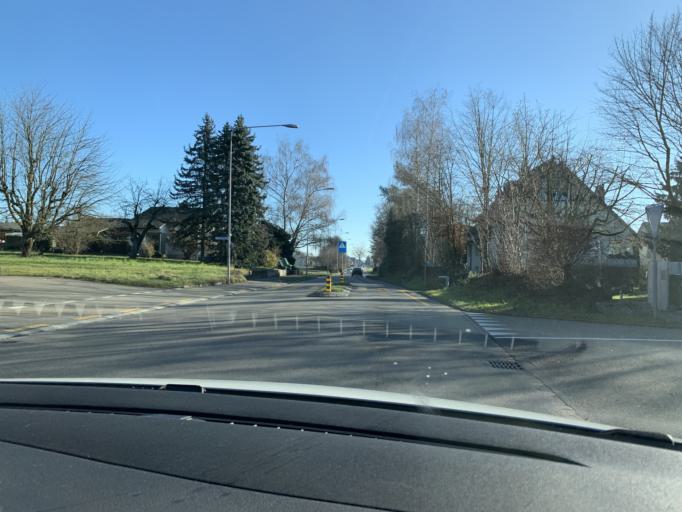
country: CH
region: Zurich
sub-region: Bezirk Dielsdorf
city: Sonnhalde
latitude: 47.4465
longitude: 8.4676
